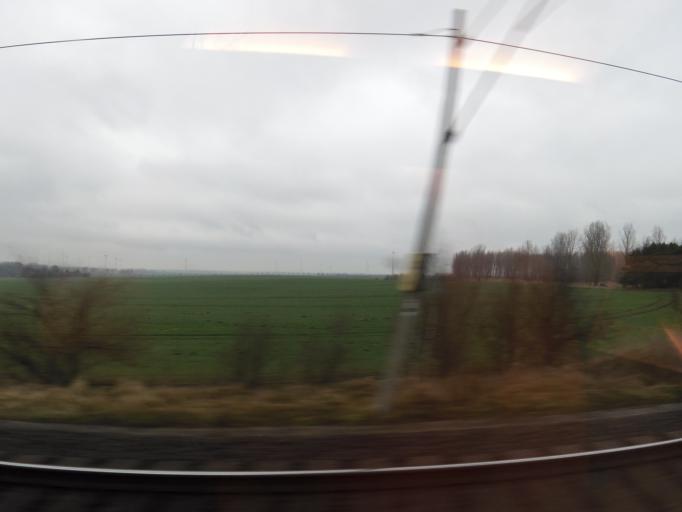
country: DE
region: Saxony-Anhalt
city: Seehausen
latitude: 52.1401
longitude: 11.2839
